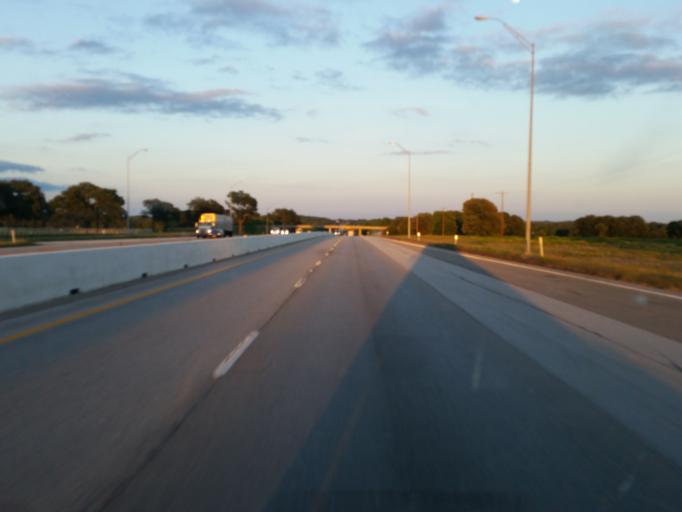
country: US
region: Texas
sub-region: Van Zandt County
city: Van
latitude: 32.4921
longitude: -95.5571
